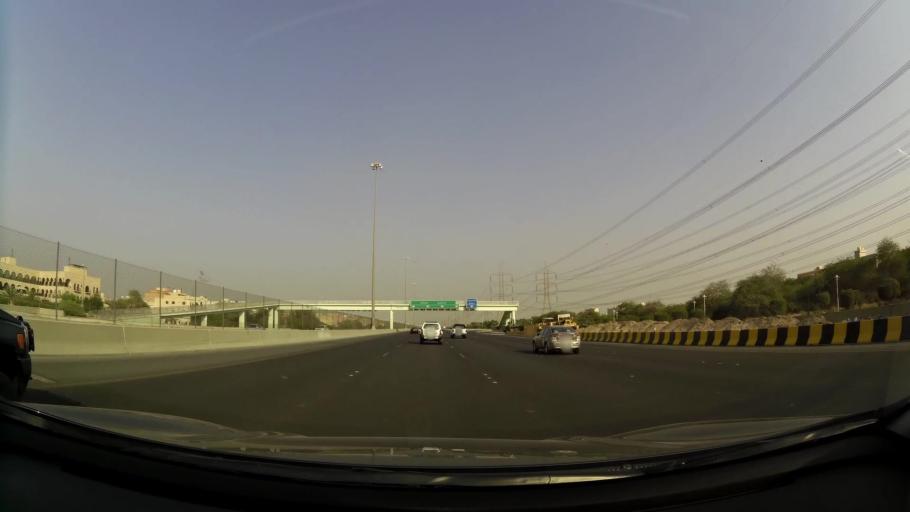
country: KW
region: Al Asimah
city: Ar Rabiyah
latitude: 29.2974
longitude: 47.8891
